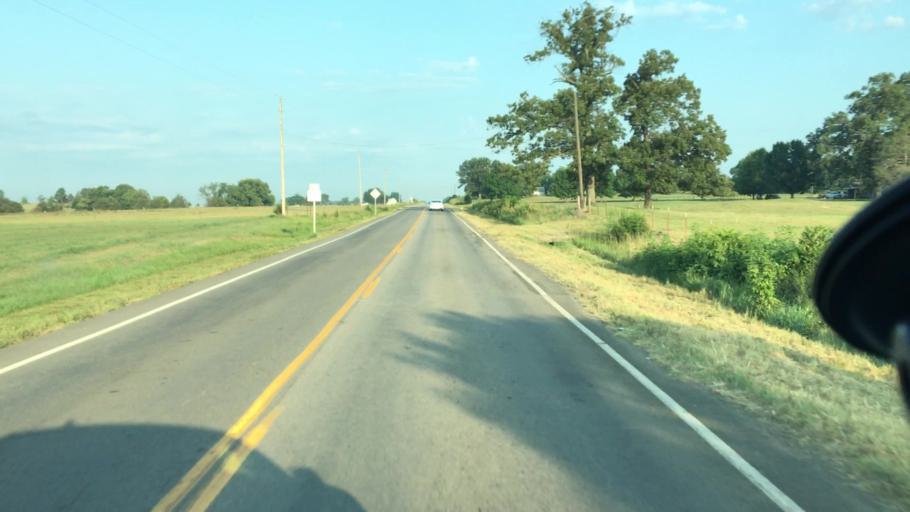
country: US
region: Arkansas
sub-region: Johnson County
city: Clarksville
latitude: 35.3786
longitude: -93.5317
